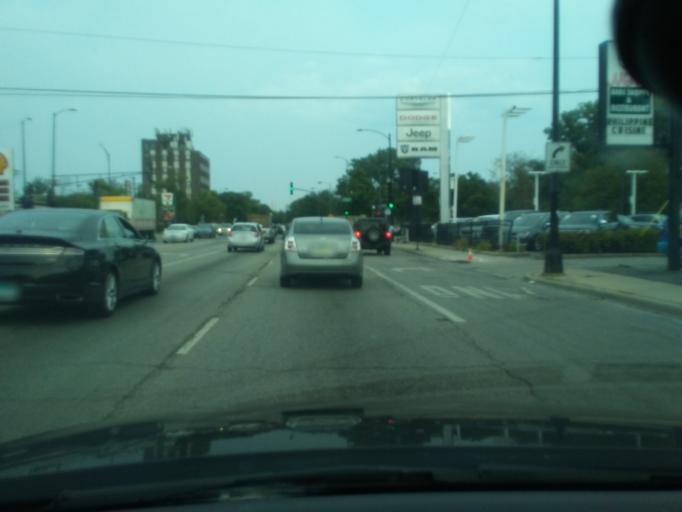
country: US
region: Illinois
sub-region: Cook County
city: Lincolnwood
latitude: 41.9904
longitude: -87.6905
